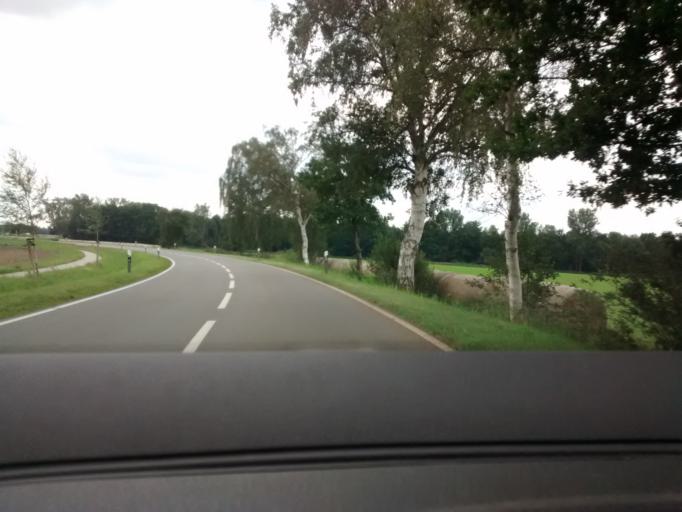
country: DE
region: Lower Saxony
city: Scharnebeck
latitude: 53.3223
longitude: 10.5042
